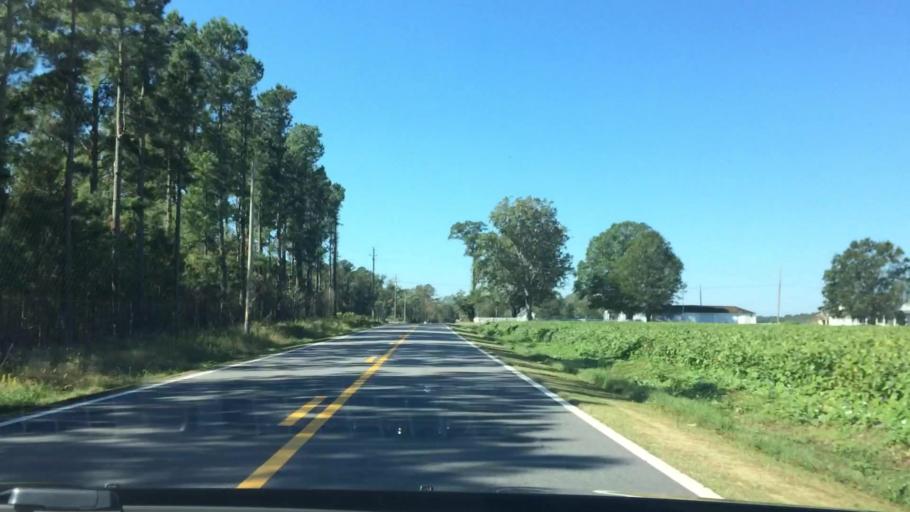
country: US
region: North Carolina
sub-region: Pitt County
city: Winterville
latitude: 35.5193
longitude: -77.4407
